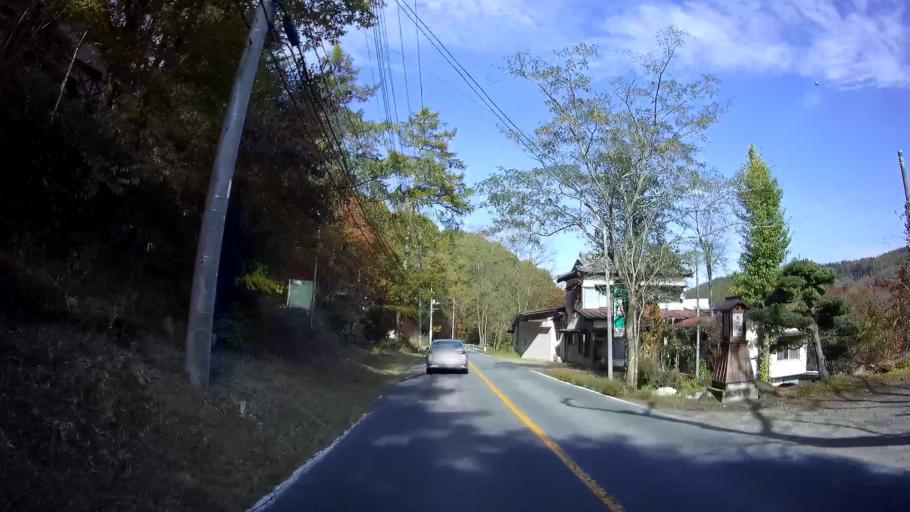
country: JP
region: Gunma
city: Nakanojomachi
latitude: 36.5010
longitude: 138.7765
